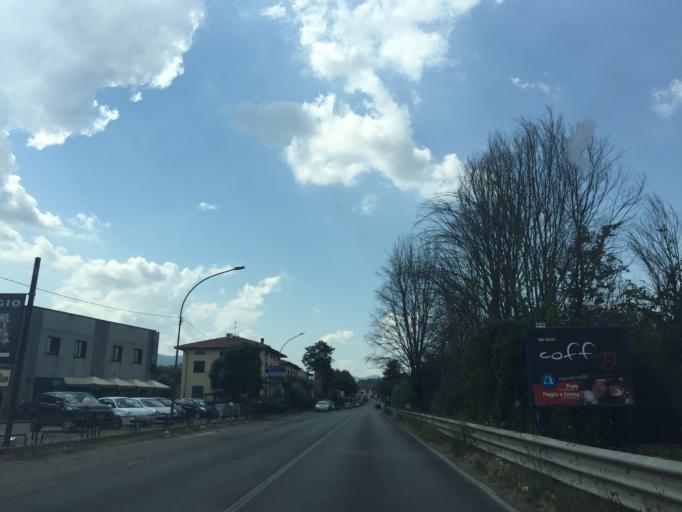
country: IT
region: Tuscany
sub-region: Provincia di Prato
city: Poggio A Caiano
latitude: 43.8136
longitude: 11.0661
